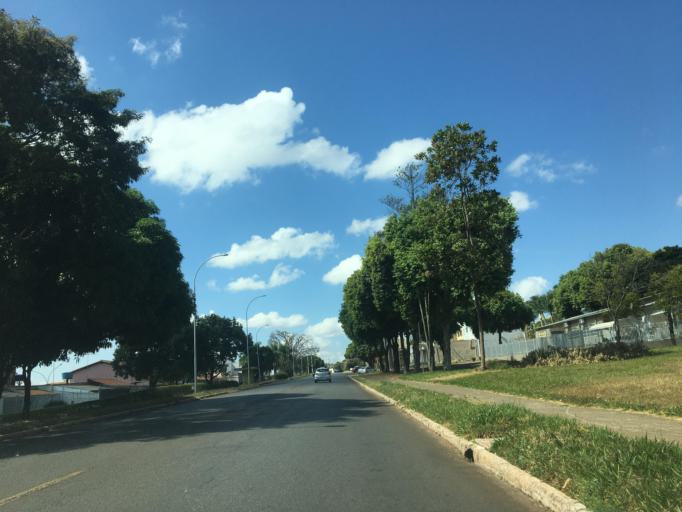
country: BR
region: Federal District
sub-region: Brasilia
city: Brasilia
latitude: -15.6454
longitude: -47.7913
